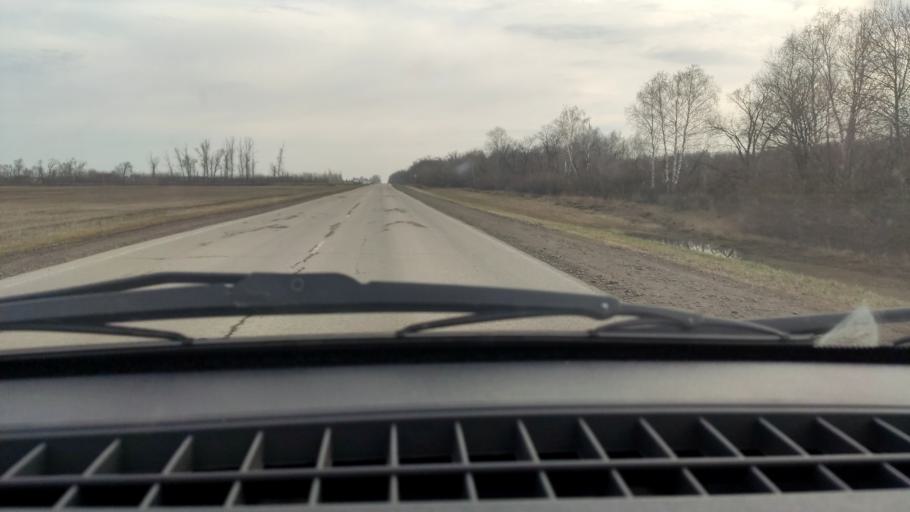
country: RU
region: Bashkortostan
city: Davlekanovo
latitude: 54.2843
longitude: 55.1130
